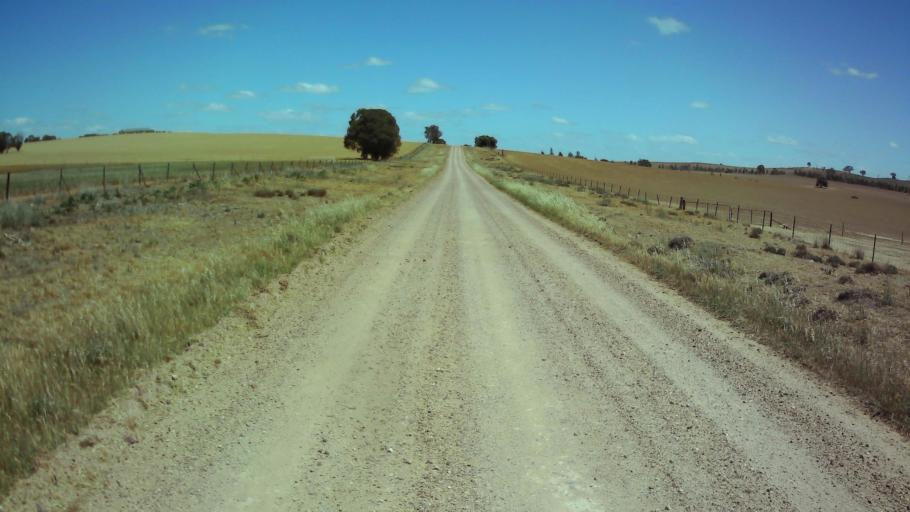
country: AU
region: New South Wales
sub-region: Weddin
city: Grenfell
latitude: -33.9457
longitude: 148.3294
